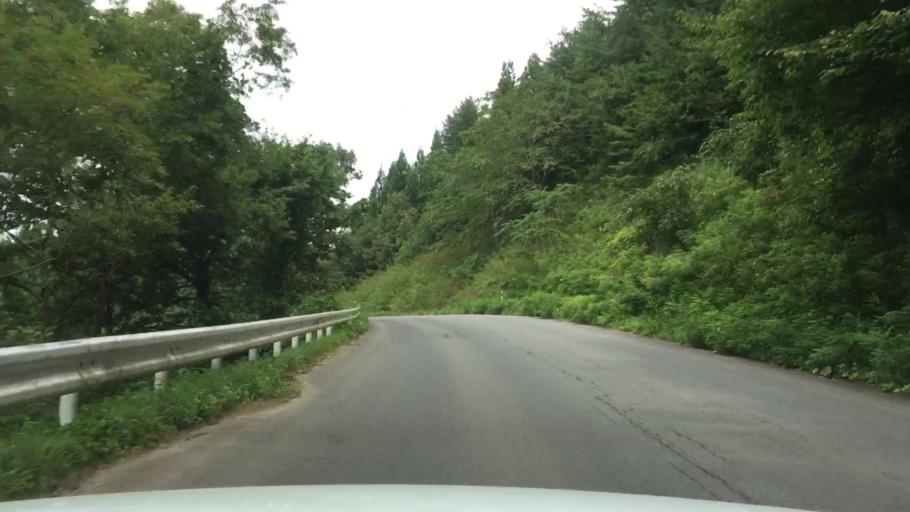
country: JP
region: Aomori
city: Shimokizukuri
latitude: 40.7191
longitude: 140.2590
